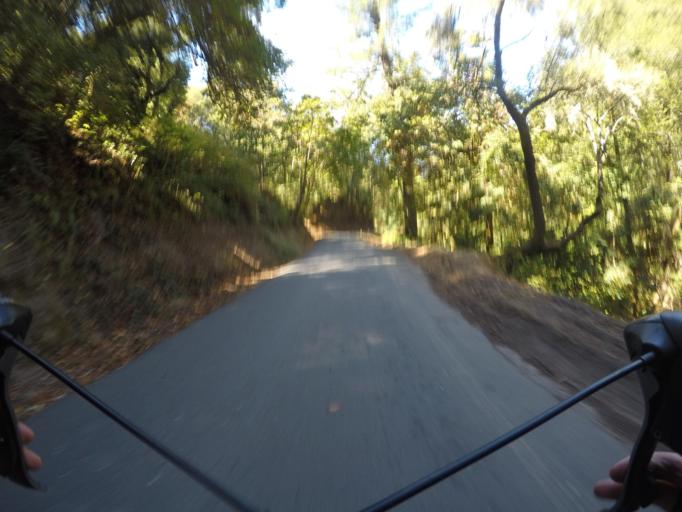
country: US
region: California
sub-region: San Mateo County
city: Portola Valley
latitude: 37.2922
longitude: -122.2352
